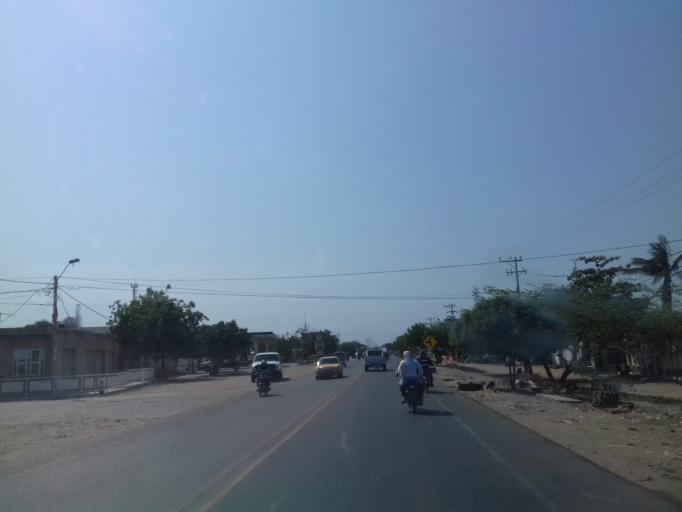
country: CO
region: La Guajira
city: Maicao
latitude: 11.3792
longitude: -72.2503
